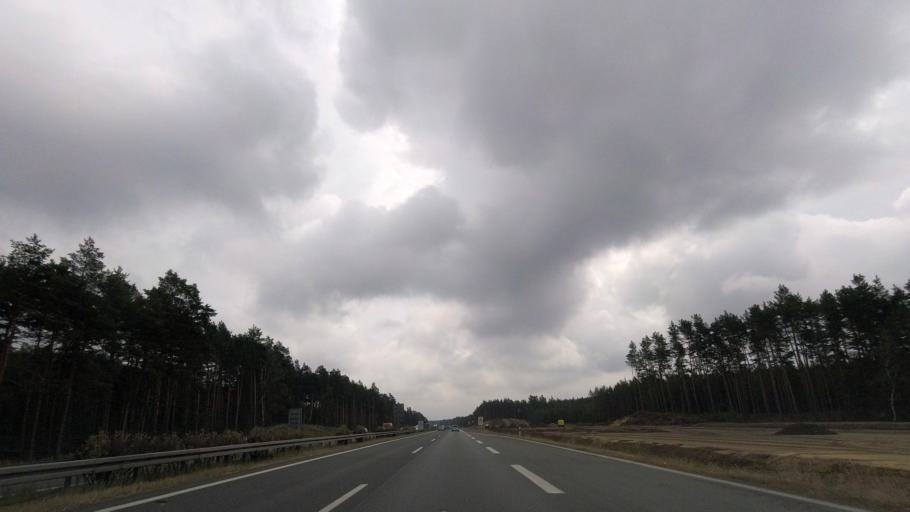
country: DE
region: Brandenburg
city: Birkenwerder
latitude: 52.6887
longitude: 13.3238
